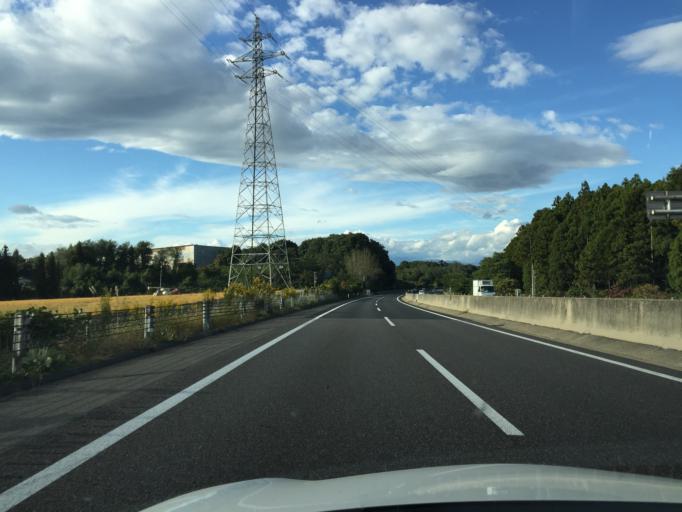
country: JP
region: Fukushima
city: Sukagawa
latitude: 37.3081
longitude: 140.3457
